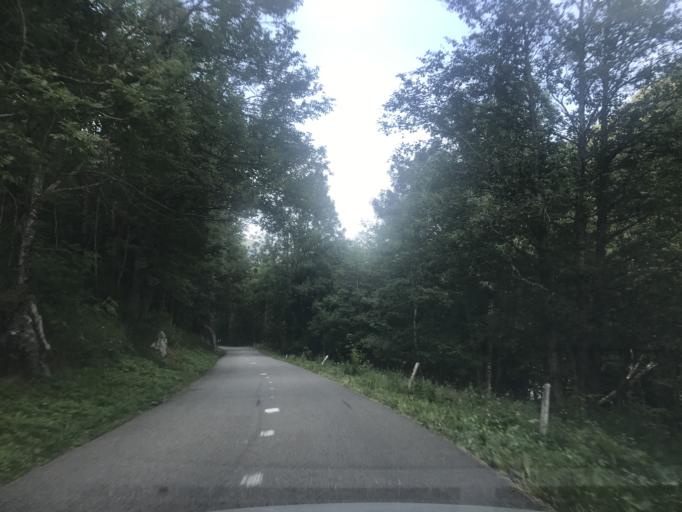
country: FR
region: Rhone-Alpes
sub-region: Departement de la Savoie
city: Saint-Etienne-de-Cuines
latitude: 45.2781
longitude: 6.2097
